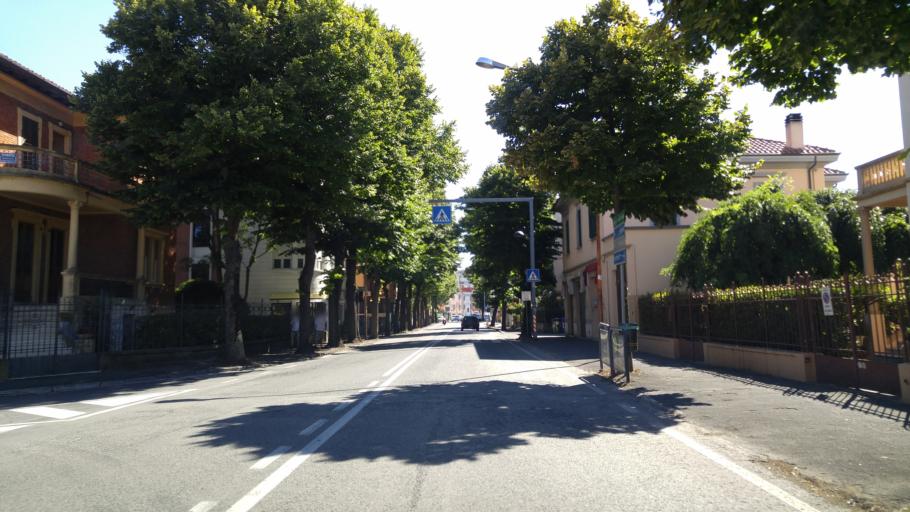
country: IT
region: The Marches
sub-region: Provincia di Pesaro e Urbino
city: Pesaro
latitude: 43.9151
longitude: 12.9100
